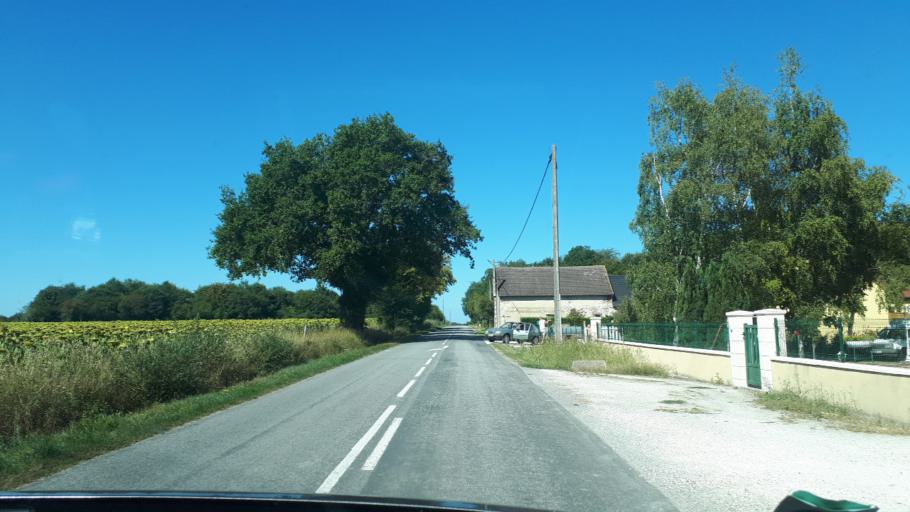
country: FR
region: Centre
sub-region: Departement du Loiret
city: Autry-le-Chatel
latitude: 47.5948
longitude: 2.6197
